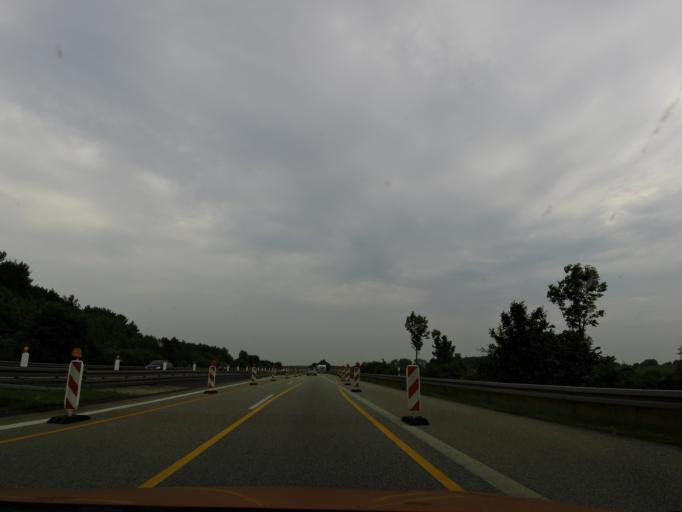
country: DE
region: Mecklenburg-Vorpommern
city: Bobitz
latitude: 53.8389
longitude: 11.3708
